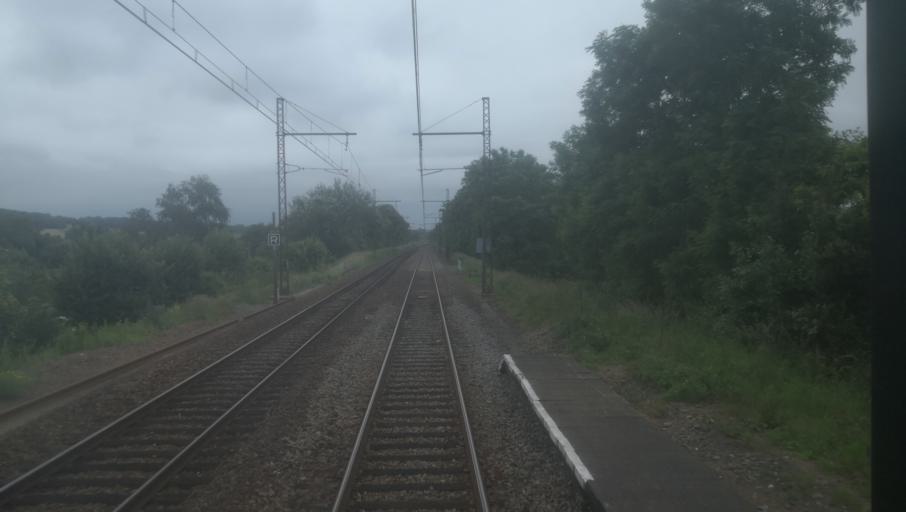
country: FR
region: Centre
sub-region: Departement de l'Indre
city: Le Pechereau
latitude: 46.5176
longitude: 1.5039
